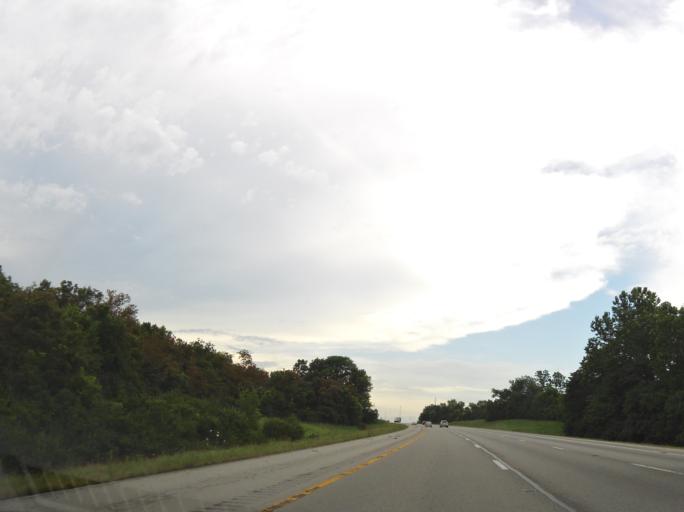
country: US
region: Kentucky
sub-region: Madison County
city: Richmond
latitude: 37.6633
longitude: -84.3100
